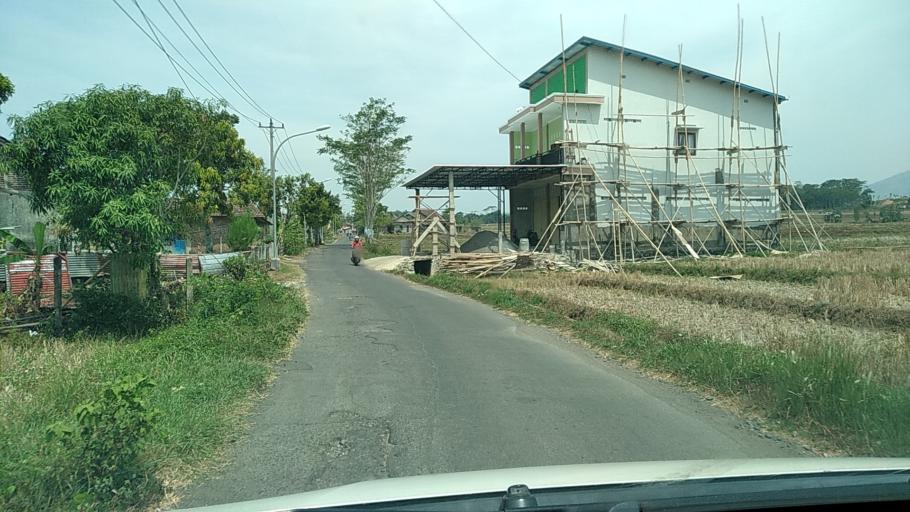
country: ID
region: Central Java
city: Ungaran
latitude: -7.0791
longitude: 110.3240
